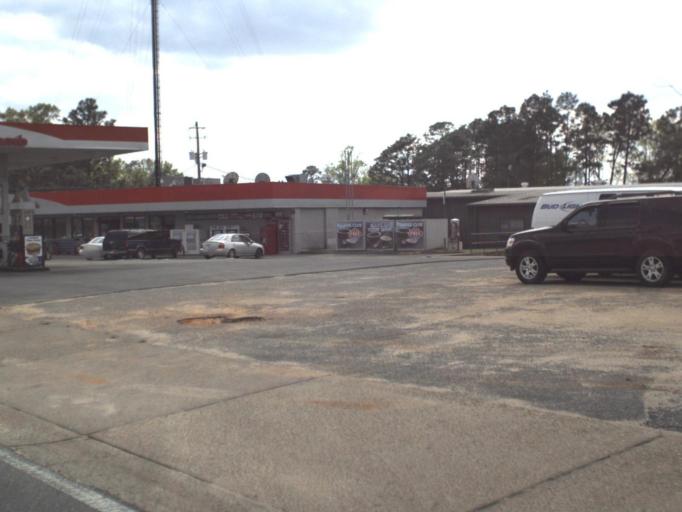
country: US
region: Florida
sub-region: Okaloosa County
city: Crestview
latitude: 30.7737
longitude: -86.5647
